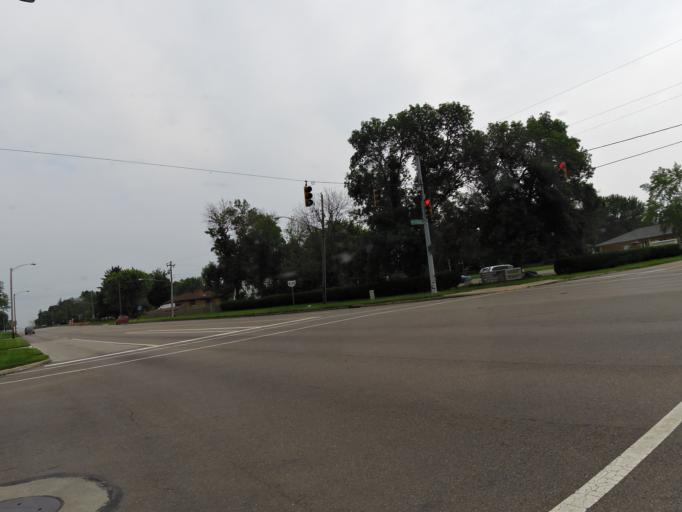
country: US
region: Ohio
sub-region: Montgomery County
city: Riverside
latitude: 39.7359
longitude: -84.1218
